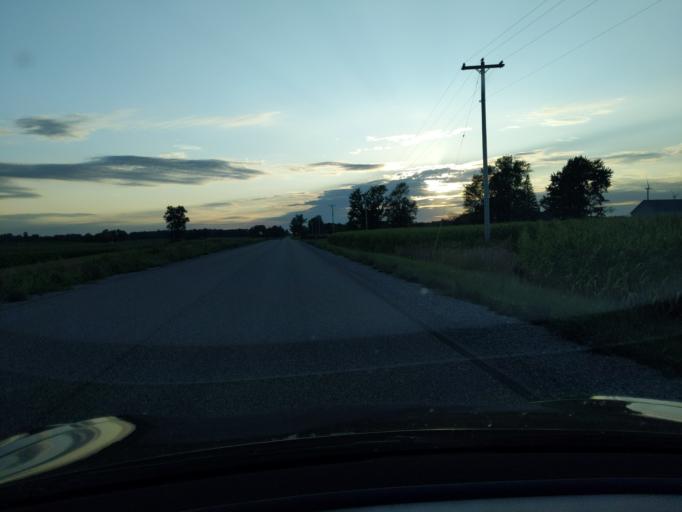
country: US
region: Michigan
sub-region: Gratiot County
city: Saint Louis
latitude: 43.3788
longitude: -84.5657
